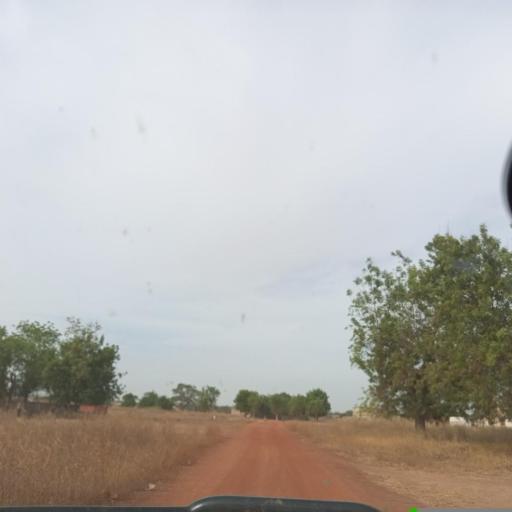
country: ML
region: Koulikoro
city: Koulikoro
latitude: 13.1115
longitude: -7.6539
